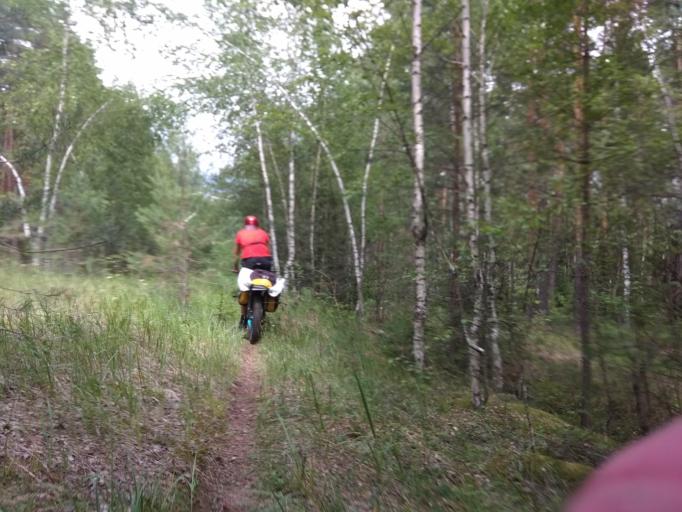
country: RU
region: Moskovskaya
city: Misheronskiy
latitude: 55.6963
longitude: 39.7158
